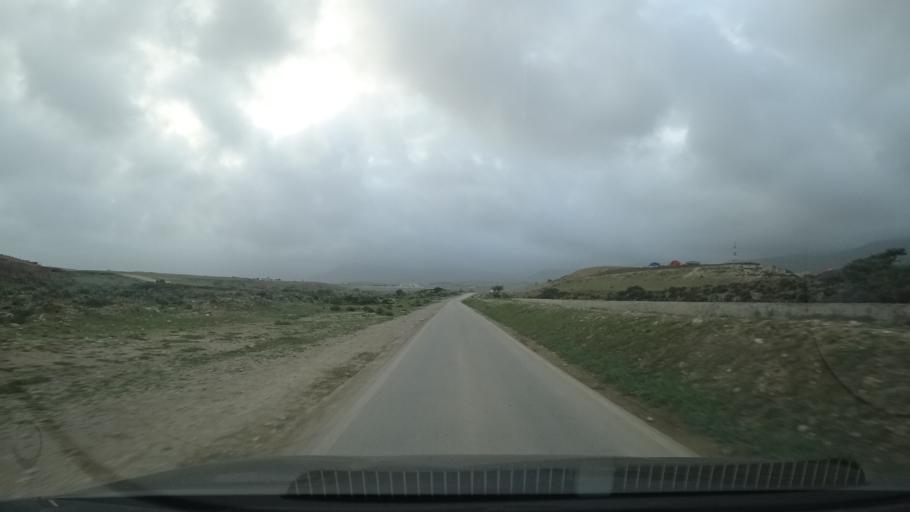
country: OM
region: Zufar
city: Salalah
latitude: 17.1056
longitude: 54.2306
